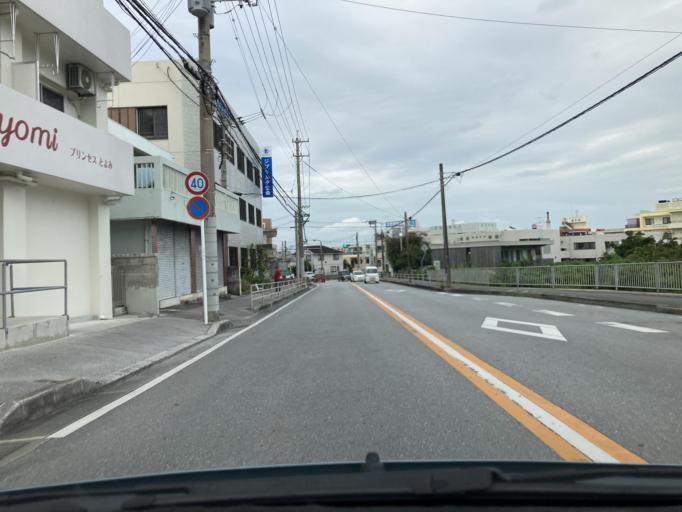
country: JP
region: Okinawa
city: Tomigusuku
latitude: 26.1884
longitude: 127.6806
